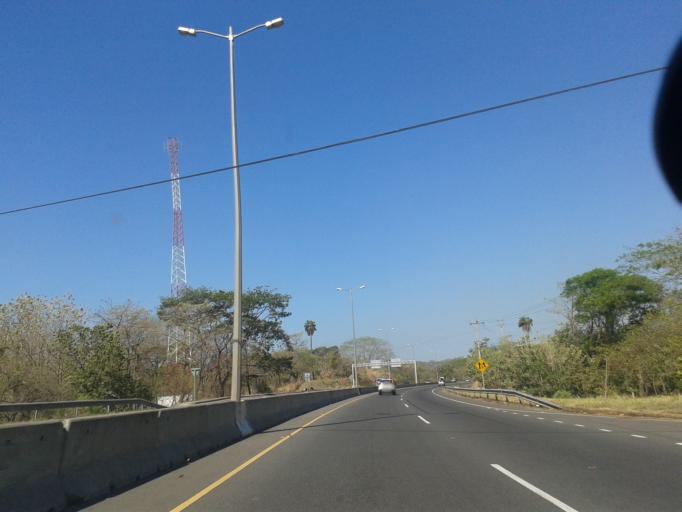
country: CR
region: Alajuela
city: Orotina
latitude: 9.8855
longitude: -84.5837
